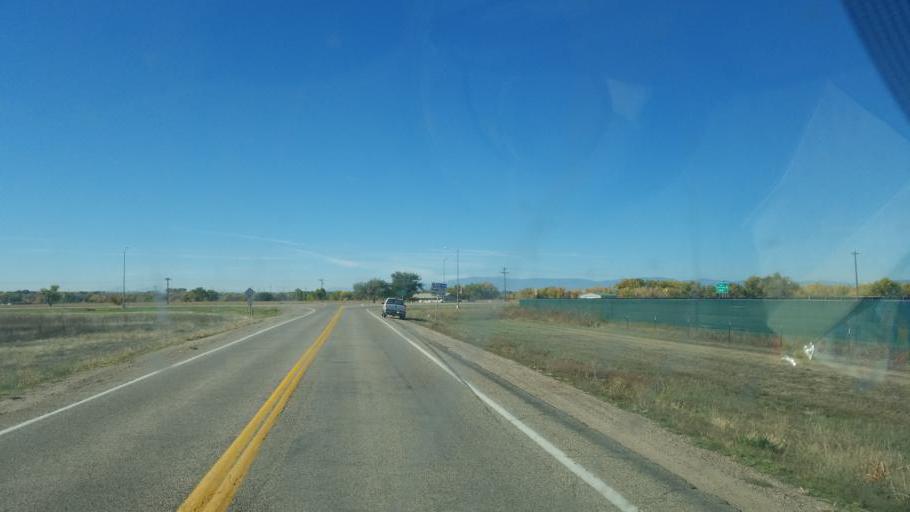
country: US
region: Colorado
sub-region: Pueblo County
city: Pueblo
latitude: 38.2623
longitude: -104.3656
